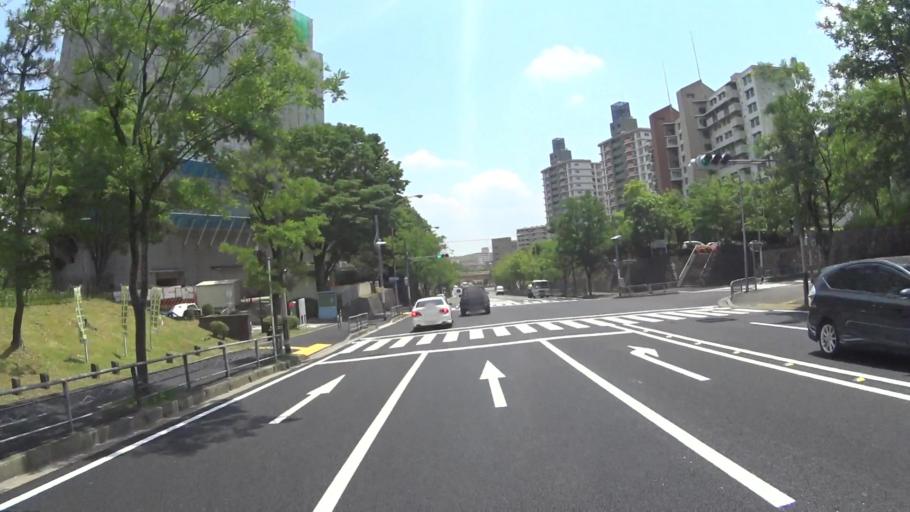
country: JP
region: Kyoto
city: Muko
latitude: 34.9662
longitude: 135.6715
